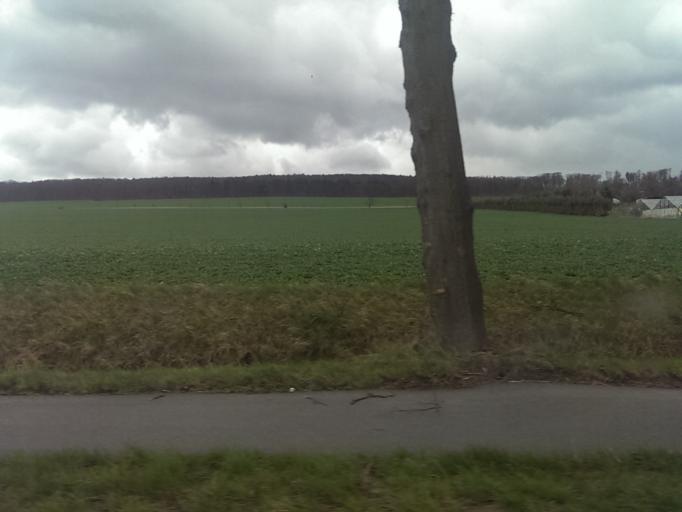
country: DE
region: Lower Saxony
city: Hildesheim
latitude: 52.1478
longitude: 9.9915
